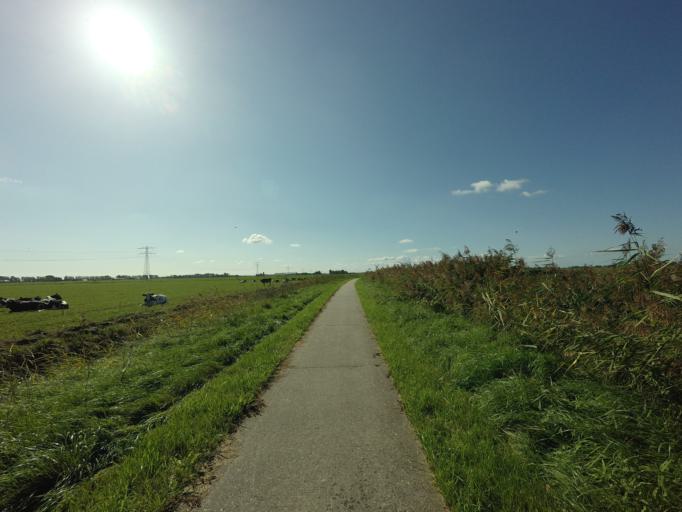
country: NL
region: Friesland
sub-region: Gemeente Boarnsterhim
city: Reduzum
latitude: 53.1437
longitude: 5.7646
